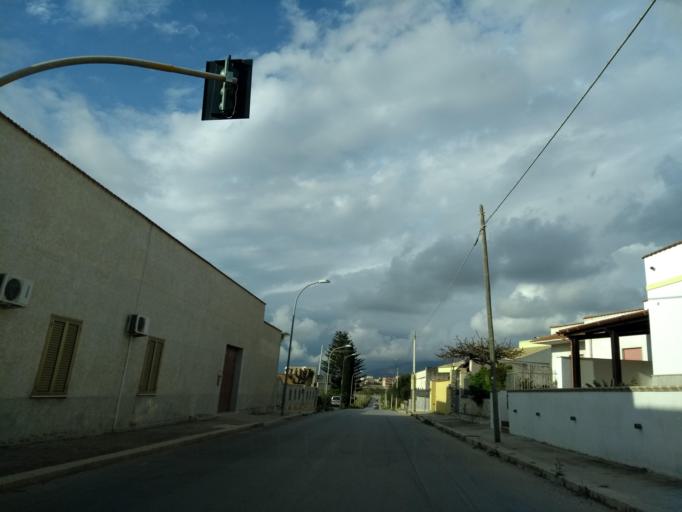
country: IT
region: Sicily
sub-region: Trapani
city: Marausa
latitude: 37.9450
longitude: 12.5123
